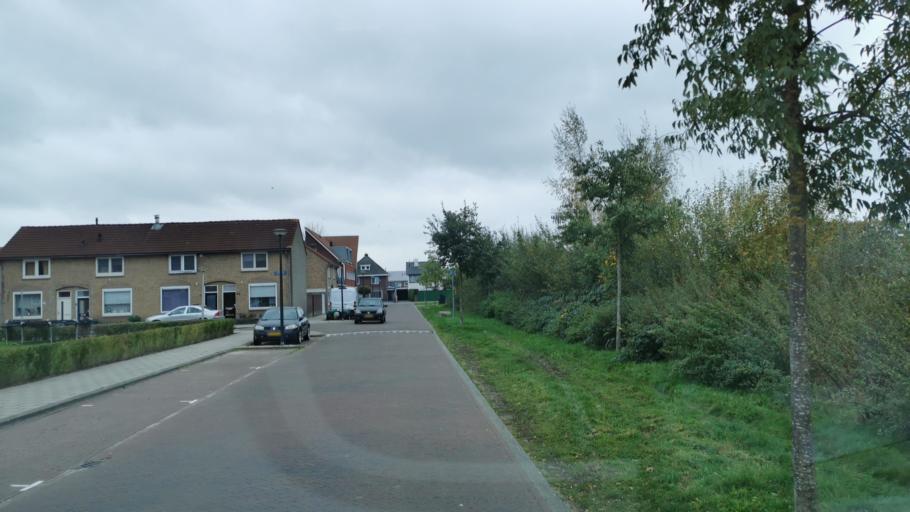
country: DE
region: North Rhine-Westphalia
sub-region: Regierungsbezirk Munster
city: Gronau
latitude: 52.2148
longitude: 6.9637
